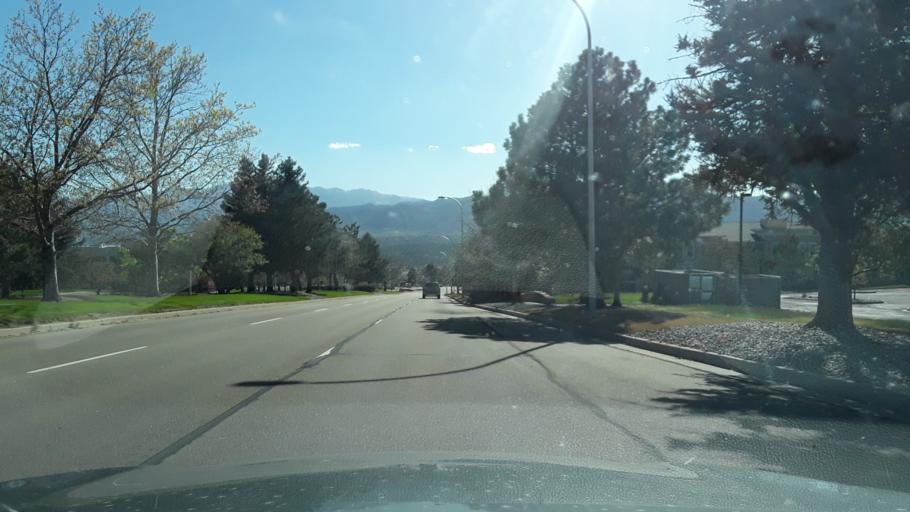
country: US
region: Colorado
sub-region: El Paso County
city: Air Force Academy
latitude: 38.9595
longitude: -104.7926
